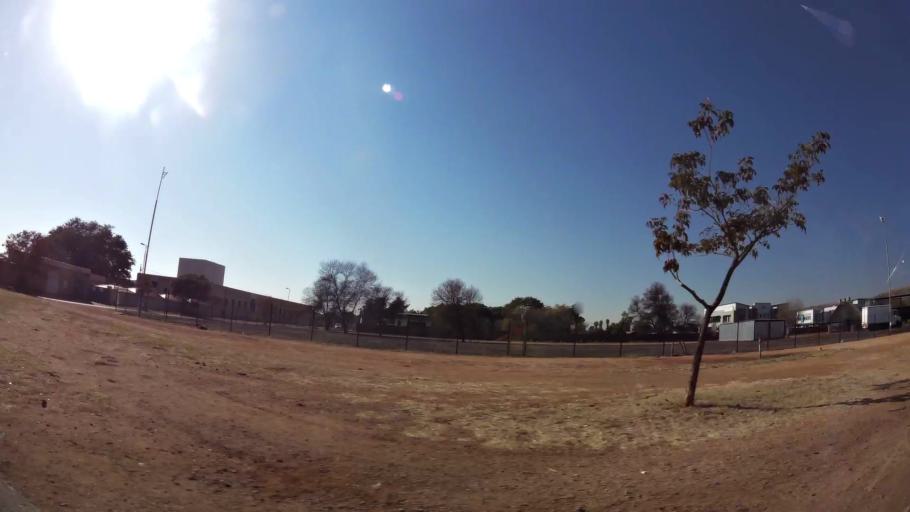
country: ZA
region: Gauteng
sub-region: City of Tshwane Metropolitan Municipality
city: Pretoria
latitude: -25.6769
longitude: 28.2430
